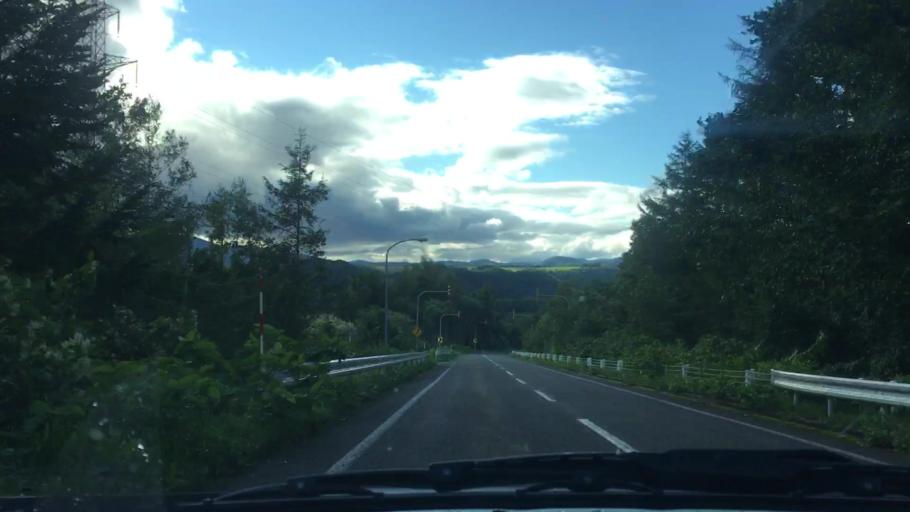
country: JP
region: Hokkaido
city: Otofuke
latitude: 43.1732
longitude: 142.9316
